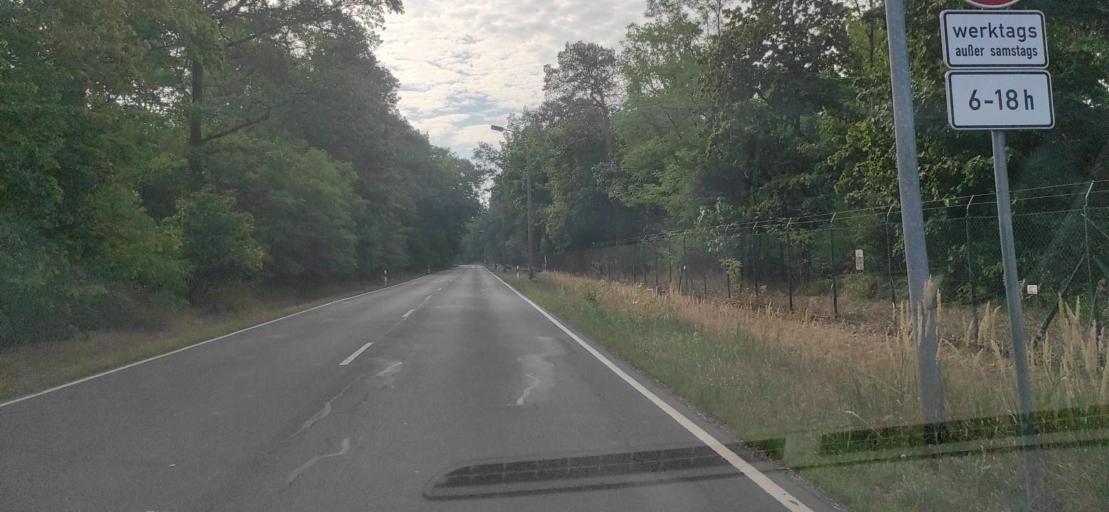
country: DE
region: Brandenburg
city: Forst
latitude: 51.7243
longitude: 14.6509
